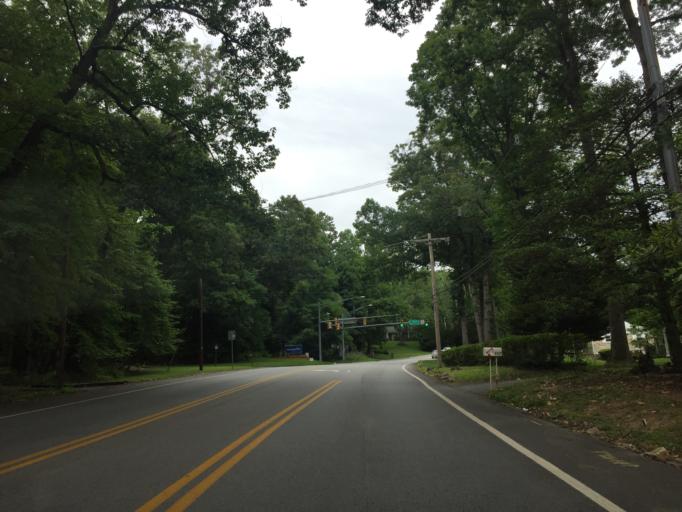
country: US
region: Maryland
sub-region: Baltimore County
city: Hampton
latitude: 39.4148
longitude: -76.5752
